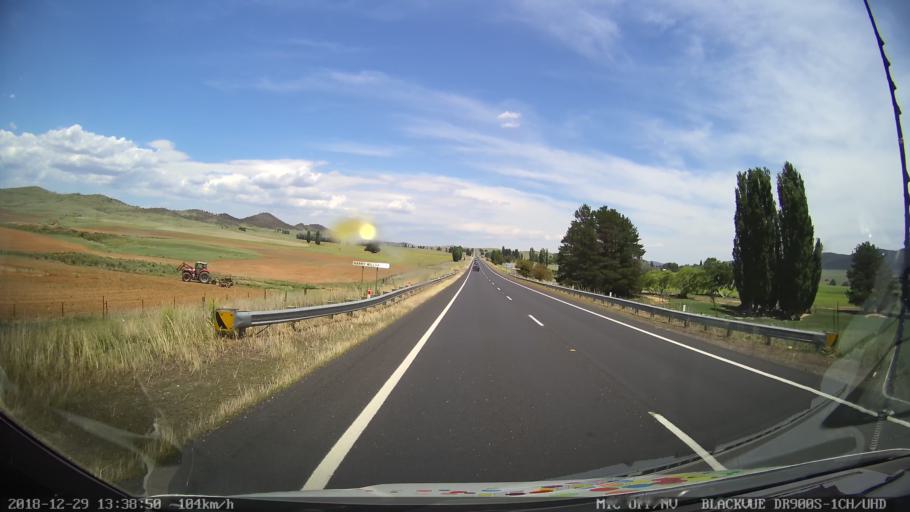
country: AU
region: New South Wales
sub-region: Cooma-Monaro
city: Cooma
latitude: -36.0041
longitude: 149.1435
